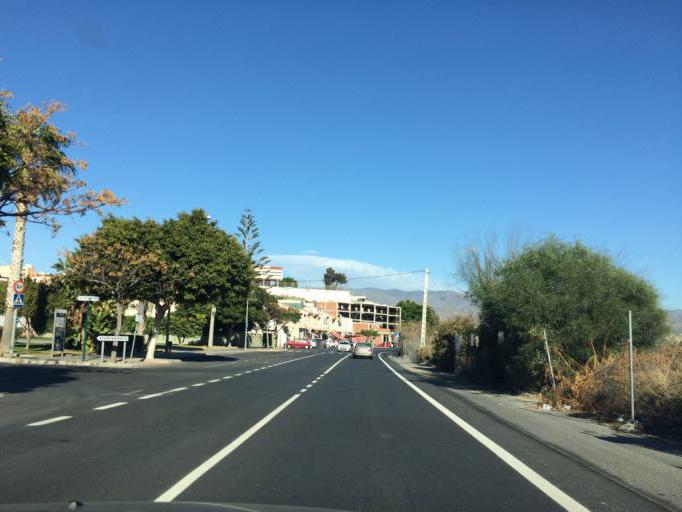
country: ES
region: Andalusia
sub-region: Provincia de Almeria
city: Huercal de Almeria
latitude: 36.8779
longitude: -2.4387
